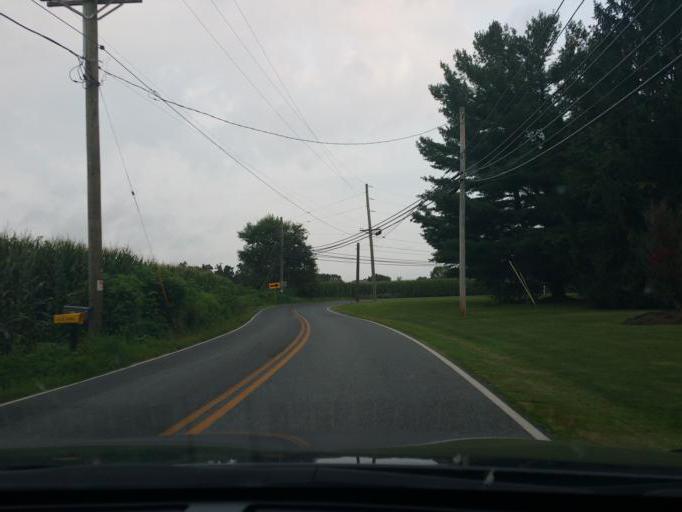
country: US
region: Maryland
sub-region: Cecil County
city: Rising Sun
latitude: 39.6420
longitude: -76.1286
